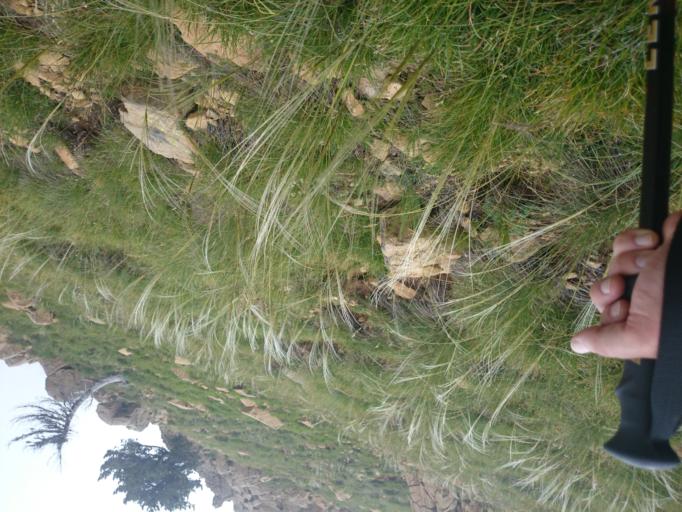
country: AL
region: Diber
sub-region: Rrethi i Dibres
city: Fushe-Lure
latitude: 41.7842
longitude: 20.1830
